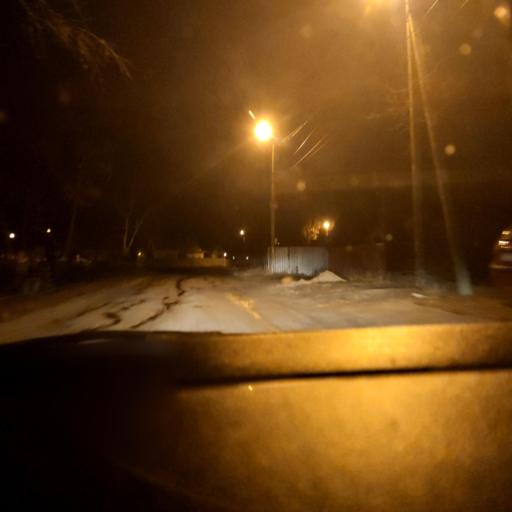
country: RU
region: Voronezj
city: Podgornoye
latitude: 51.7316
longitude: 39.1453
